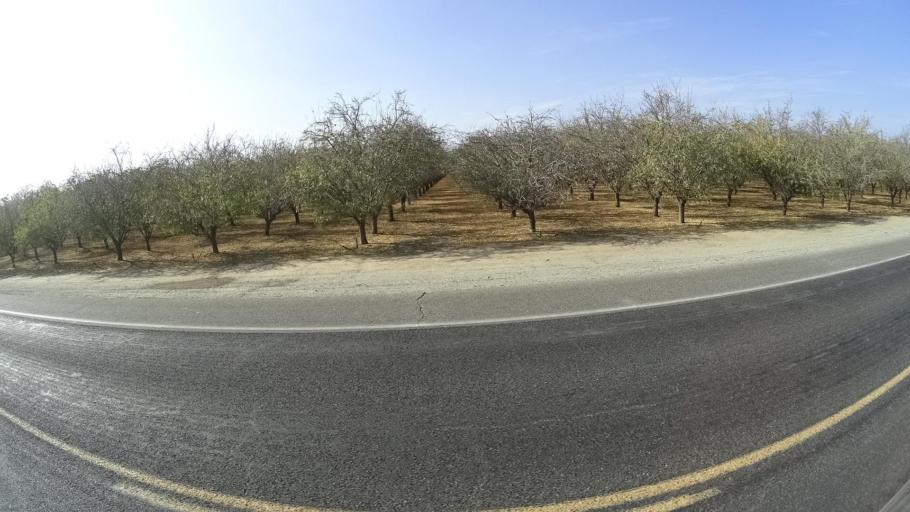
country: US
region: California
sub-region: Kern County
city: McFarland
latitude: 35.6483
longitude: -119.1956
